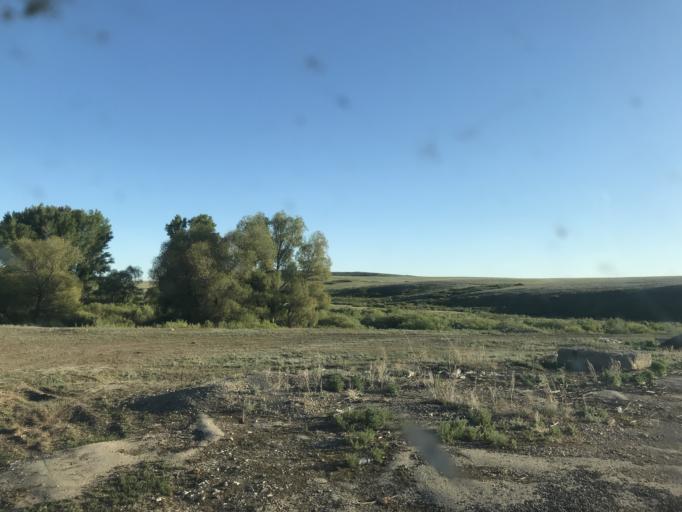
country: KZ
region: Aqtoebe
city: Aqtobe
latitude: 50.2889
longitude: 57.6799
